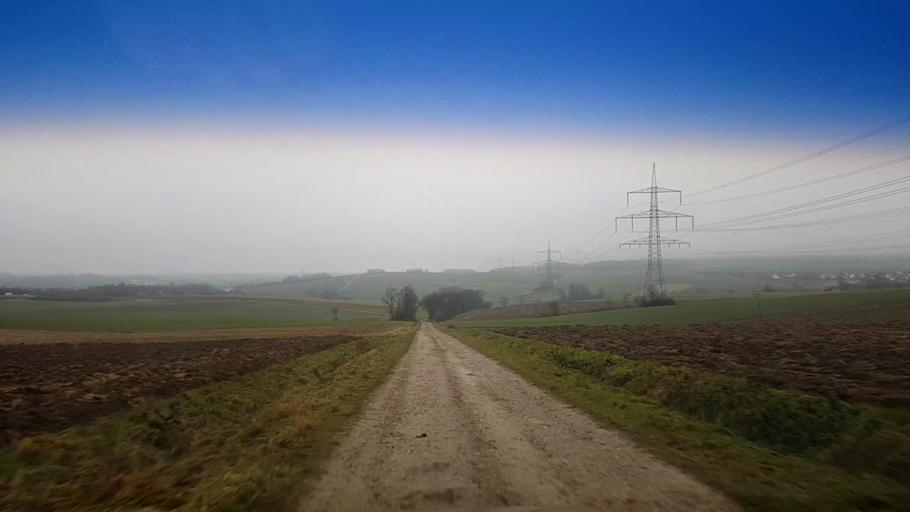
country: DE
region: Bavaria
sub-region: Upper Franconia
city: Memmelsdorf
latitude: 49.9578
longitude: 10.9781
